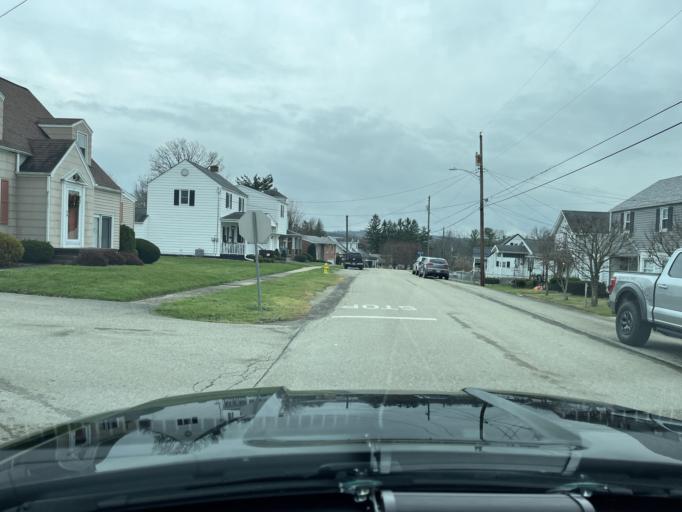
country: US
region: Pennsylvania
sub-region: Fayette County
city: South Uniontown
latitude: 39.8931
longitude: -79.7494
